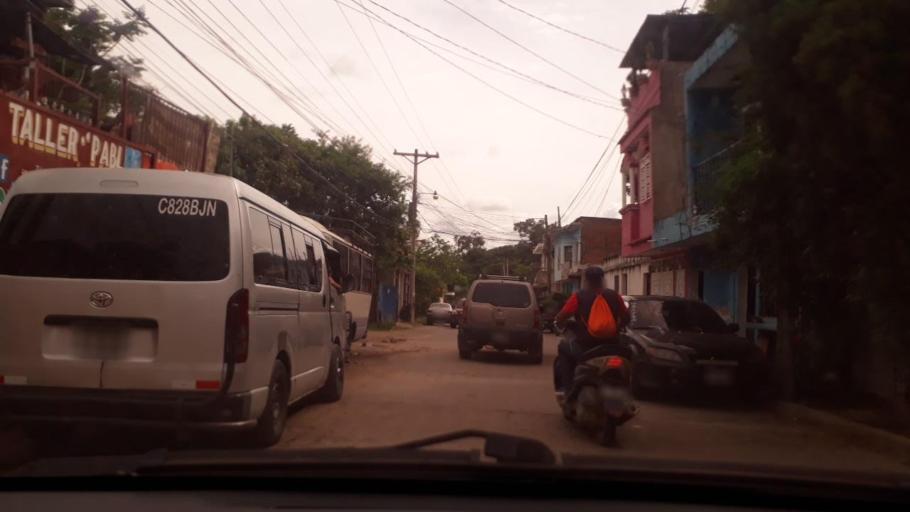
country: GT
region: Jutiapa
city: Jutiapa
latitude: 14.3000
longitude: -89.8926
